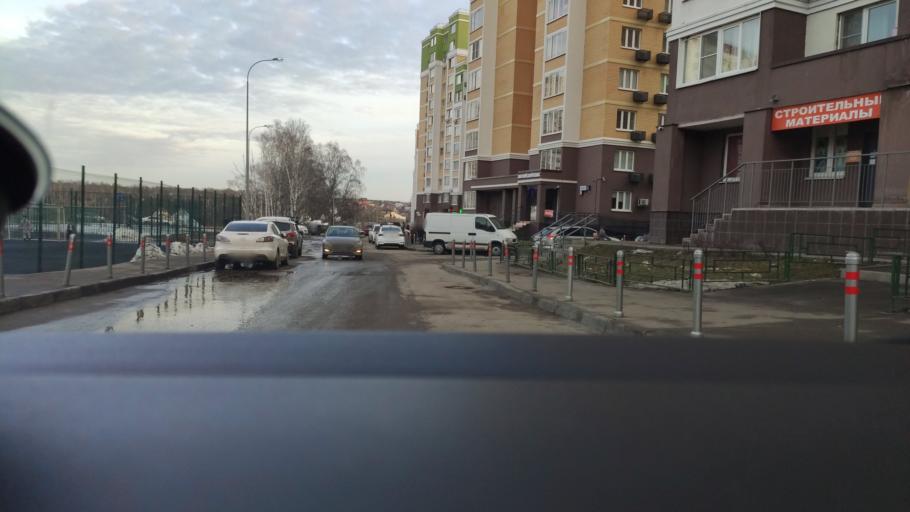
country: RU
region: Moskovskaya
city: Vidnoye
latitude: 55.5345
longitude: 37.7231
